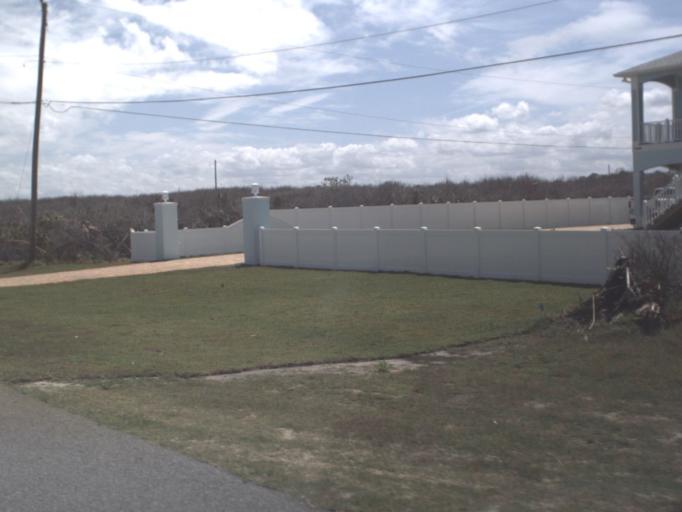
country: US
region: Florida
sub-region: Flagler County
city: Palm Coast
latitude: 29.6600
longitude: -81.2096
